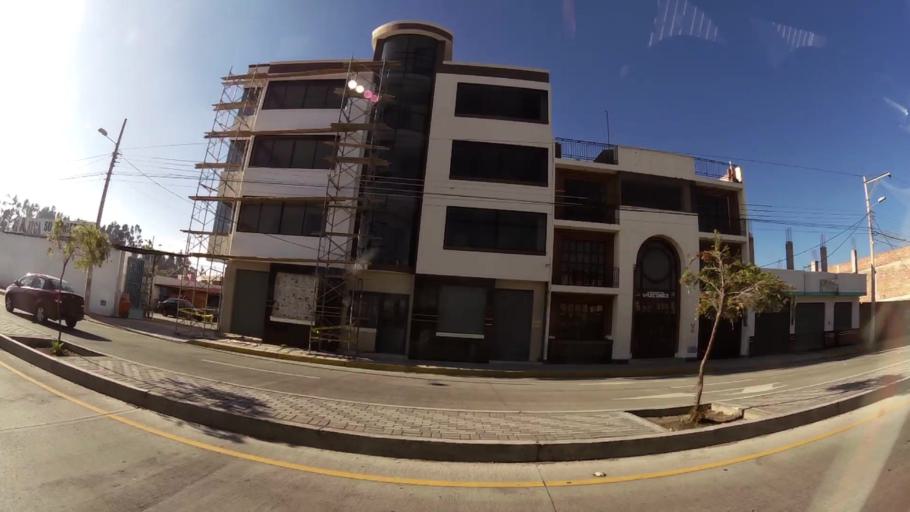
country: EC
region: Chimborazo
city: Riobamba
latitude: -1.6778
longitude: -78.6525
